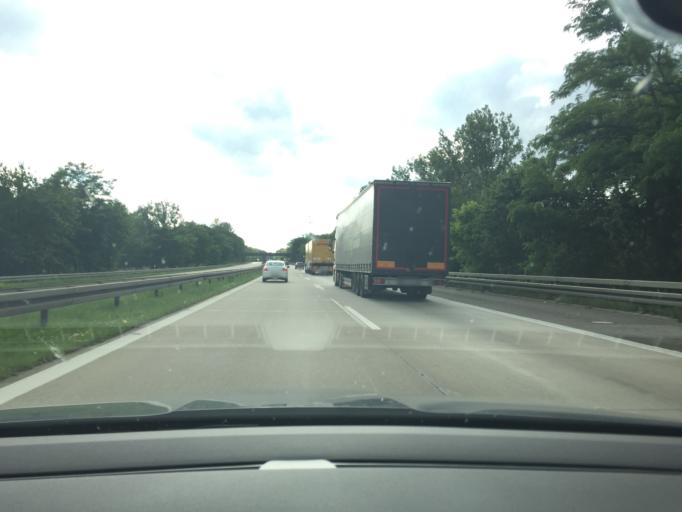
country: DE
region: Brandenburg
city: Frankfurt (Oder)
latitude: 52.3147
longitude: 14.5569
